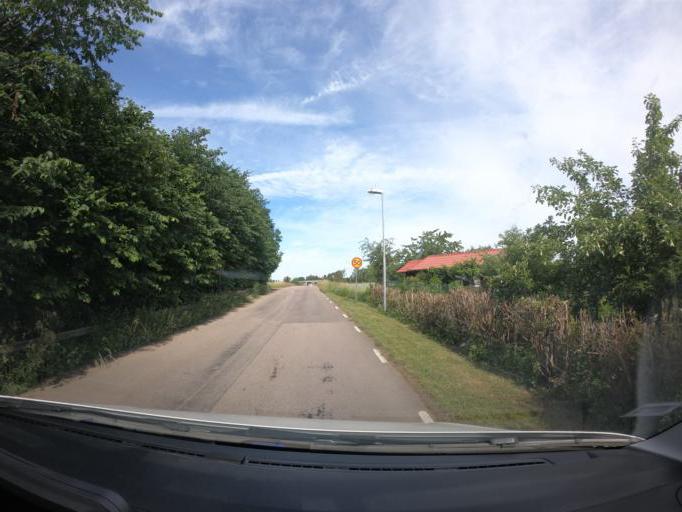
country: SE
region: Skane
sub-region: Astorps Kommun
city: Astorp
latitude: 56.1465
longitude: 12.9423
